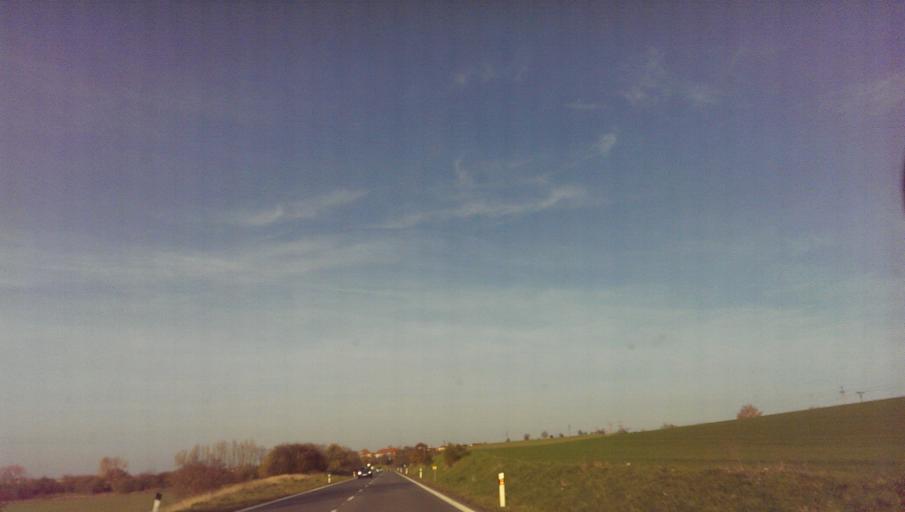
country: CZ
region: Zlin
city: Kunovice
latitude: 49.0263
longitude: 17.4556
